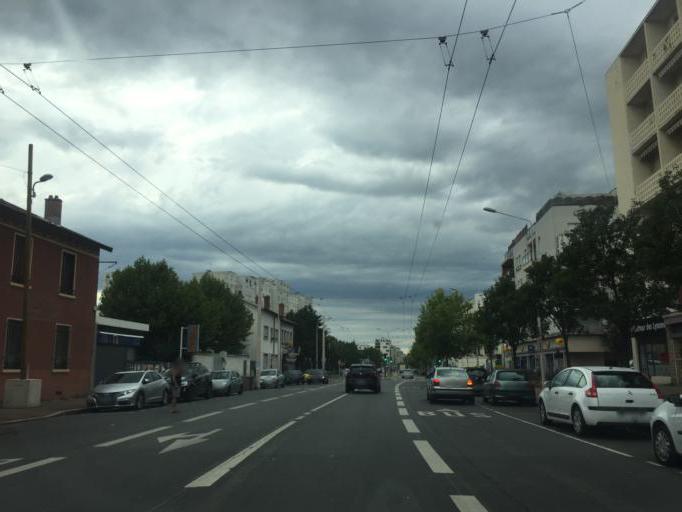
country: FR
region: Rhone-Alpes
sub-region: Departement du Rhone
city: Saint-Fons
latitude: 45.7280
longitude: 4.8778
